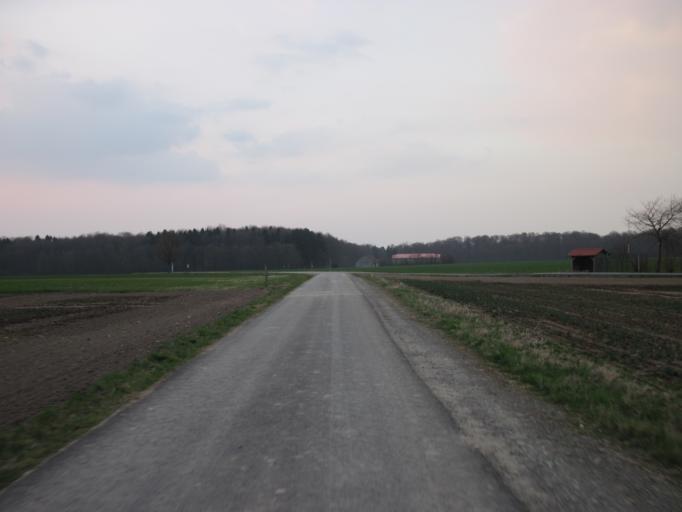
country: DE
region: North Rhine-Westphalia
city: Lichtenau
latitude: 51.6756
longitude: 8.8592
